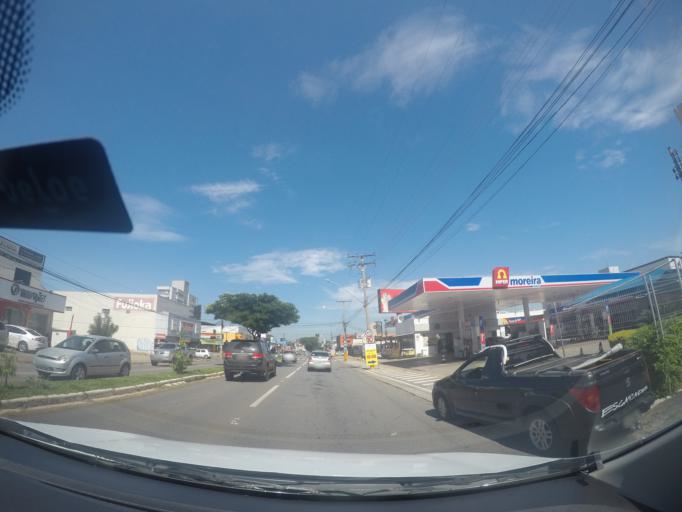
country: BR
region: Goias
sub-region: Goiania
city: Goiania
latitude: -16.7093
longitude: -49.2911
